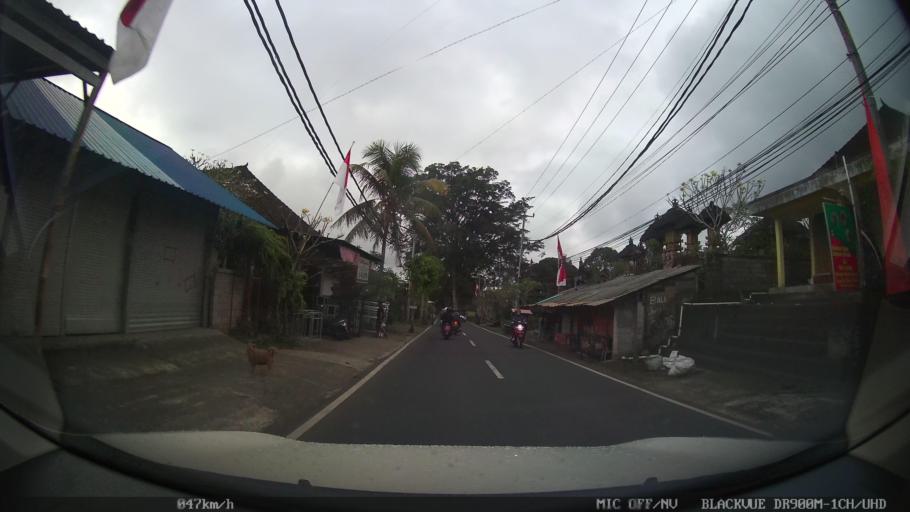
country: ID
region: Bali
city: Bayad
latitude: -8.4431
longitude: 115.2438
